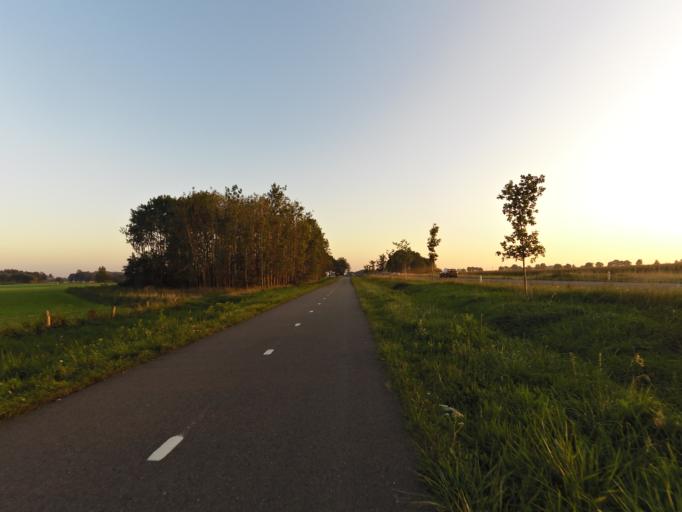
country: NL
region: Gelderland
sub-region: Gemeente Doetinchem
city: Doetinchem
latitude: 51.9382
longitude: 6.3139
